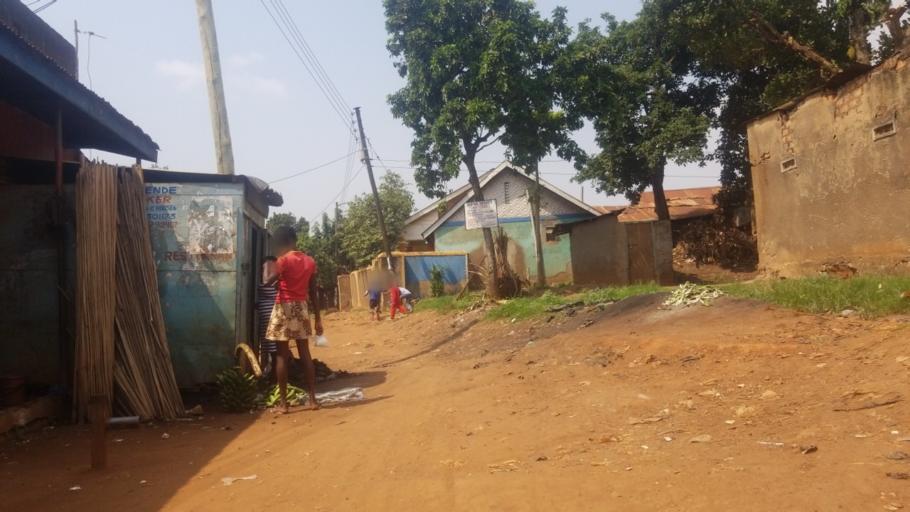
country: UG
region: Central Region
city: Kampala Central Division
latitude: 0.3401
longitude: 32.5566
